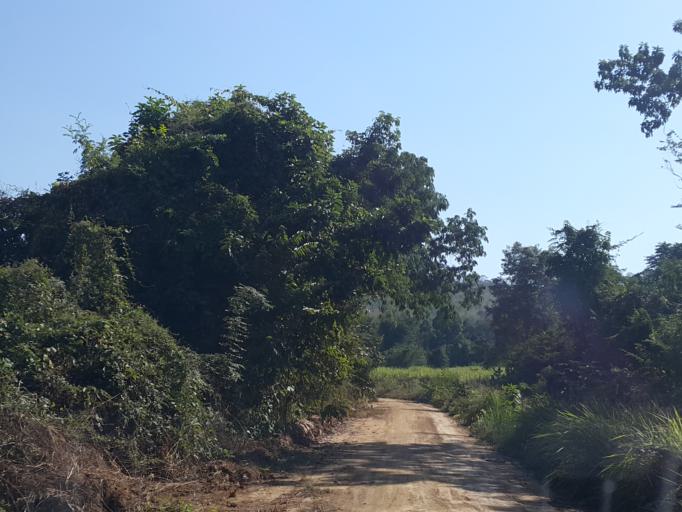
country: TH
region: Sukhothai
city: Thung Saliam
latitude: 17.3152
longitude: 99.4455
